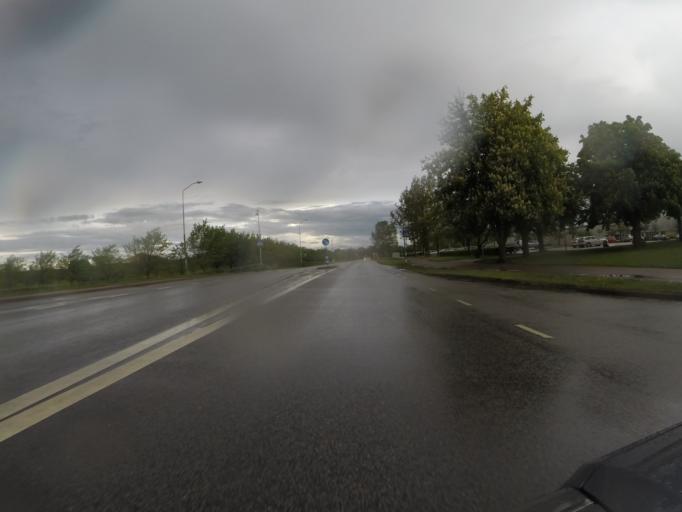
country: SE
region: Skane
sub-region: Bjuvs Kommun
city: Bjuv
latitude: 56.0757
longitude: 12.9423
